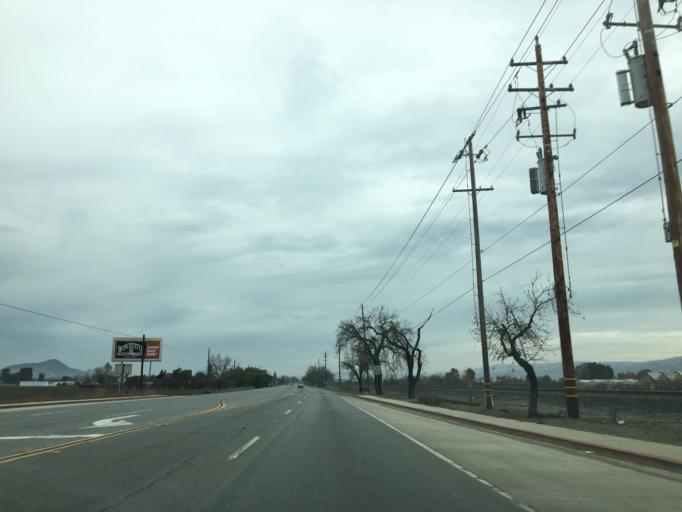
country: US
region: California
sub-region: Santa Clara County
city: San Martin
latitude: 37.0678
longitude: -121.6001
